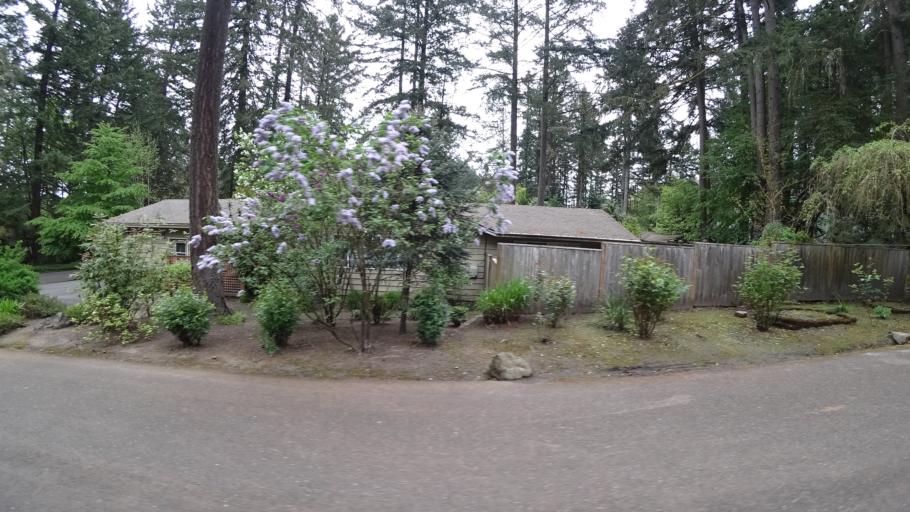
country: US
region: Oregon
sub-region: Washington County
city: Beaverton
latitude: 45.4626
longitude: -122.8200
